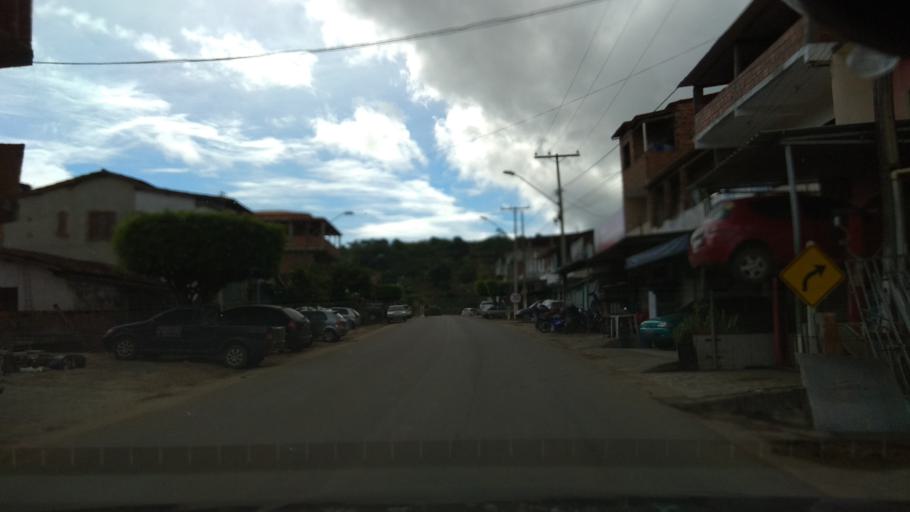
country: BR
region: Bahia
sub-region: Mutuipe
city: Mutuipe
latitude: -13.2533
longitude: -39.5705
